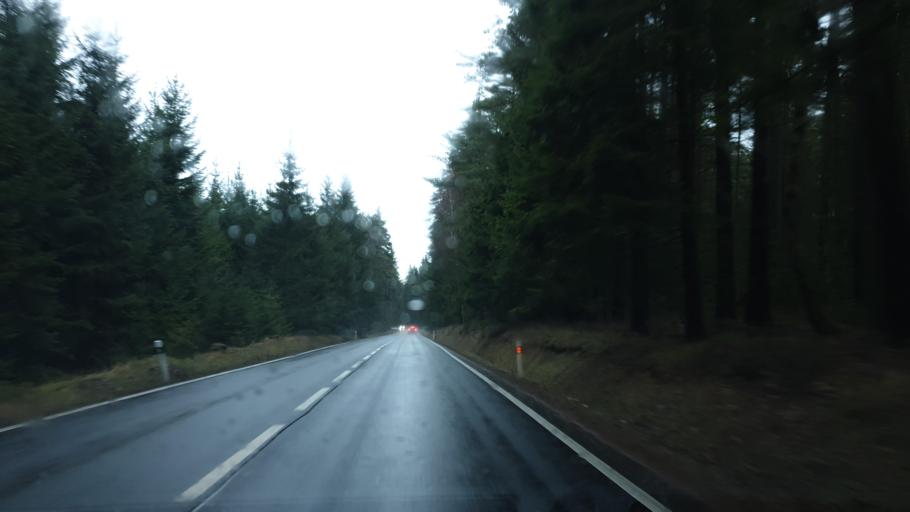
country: CZ
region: Karlovarsky
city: As
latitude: 50.2641
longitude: 12.1875
